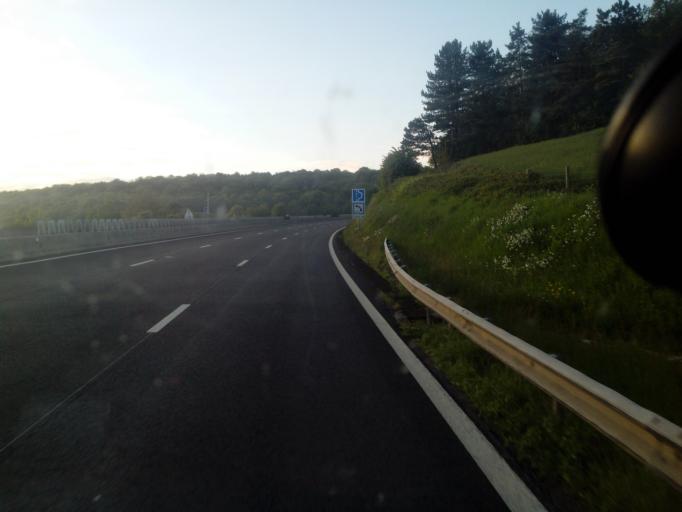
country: FR
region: Picardie
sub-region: Departement de la Somme
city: Bouttencourt
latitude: 49.9384
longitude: 1.6397
